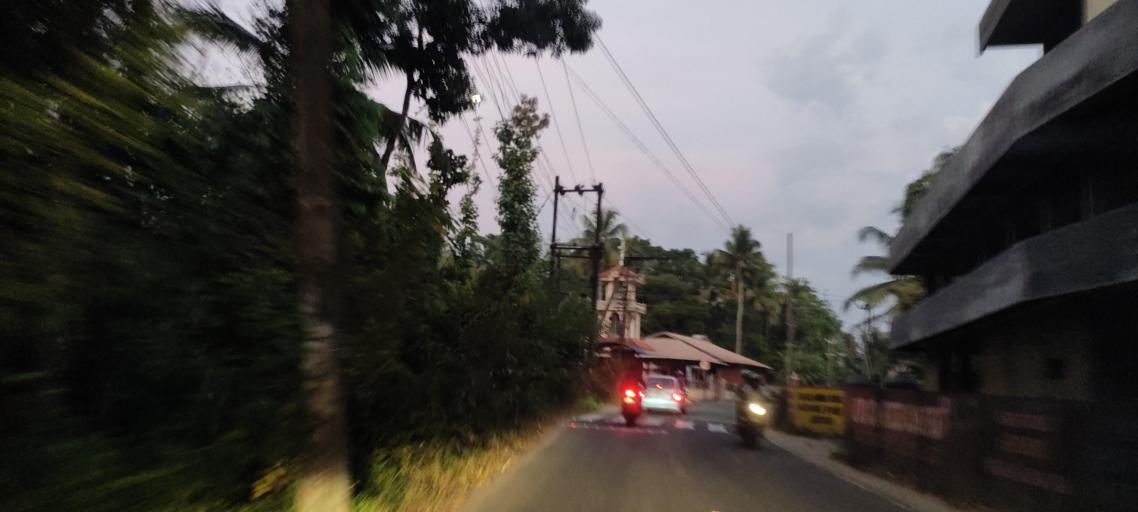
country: IN
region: Kerala
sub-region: Alappuzha
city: Kutiatodu
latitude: 9.7732
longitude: 76.3476
